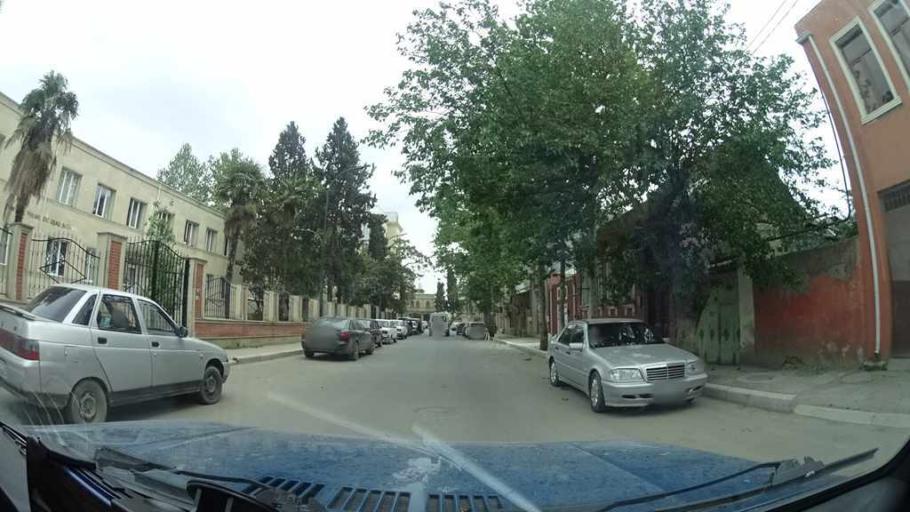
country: AZ
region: Ganja City
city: Ganja
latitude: 40.6798
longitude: 46.3604
